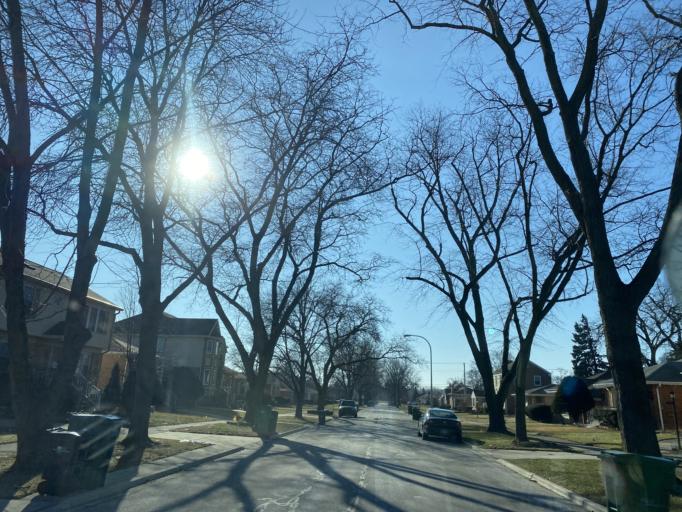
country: US
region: Illinois
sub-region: Cook County
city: Westchester
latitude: 41.8538
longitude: -87.8698
